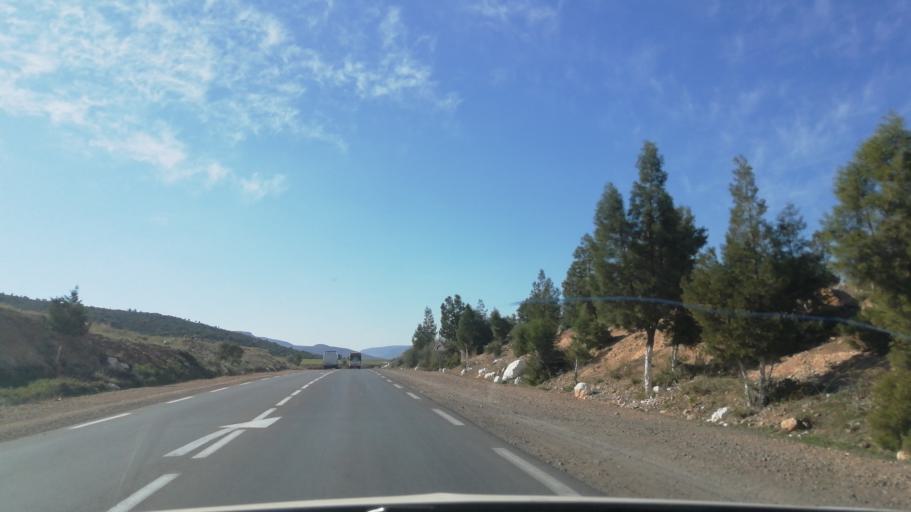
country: DZ
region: Tlemcen
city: Ouled Mimoun
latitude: 34.8875
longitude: -1.0756
